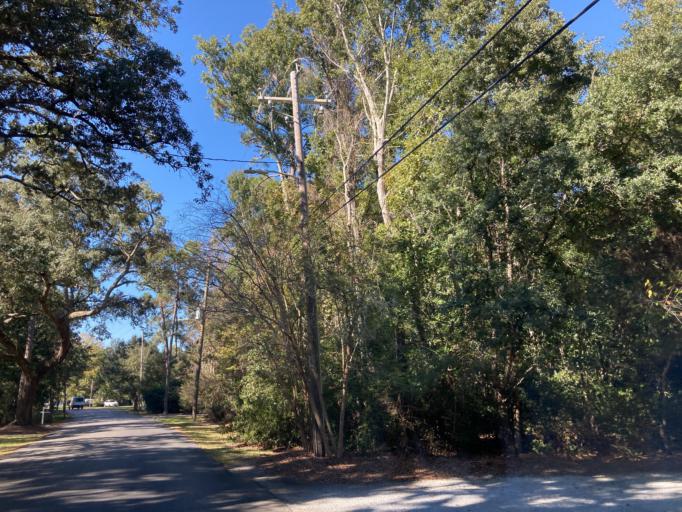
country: US
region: Mississippi
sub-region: Jackson County
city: Ocean Springs
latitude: 30.4030
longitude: -88.8174
